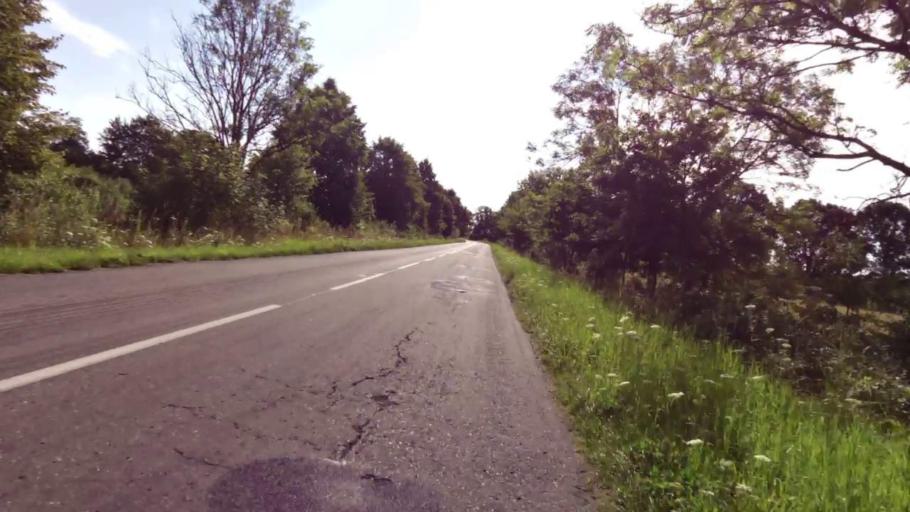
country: PL
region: West Pomeranian Voivodeship
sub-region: Powiat stargardzki
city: Marianowo
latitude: 53.3646
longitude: 15.3184
